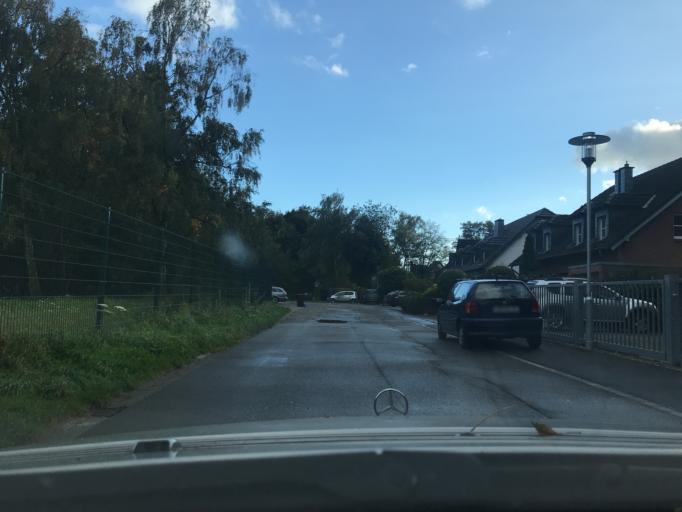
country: DE
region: North Rhine-Westphalia
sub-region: Regierungsbezirk Dusseldorf
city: Krefeld
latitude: 51.3525
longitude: 6.5775
